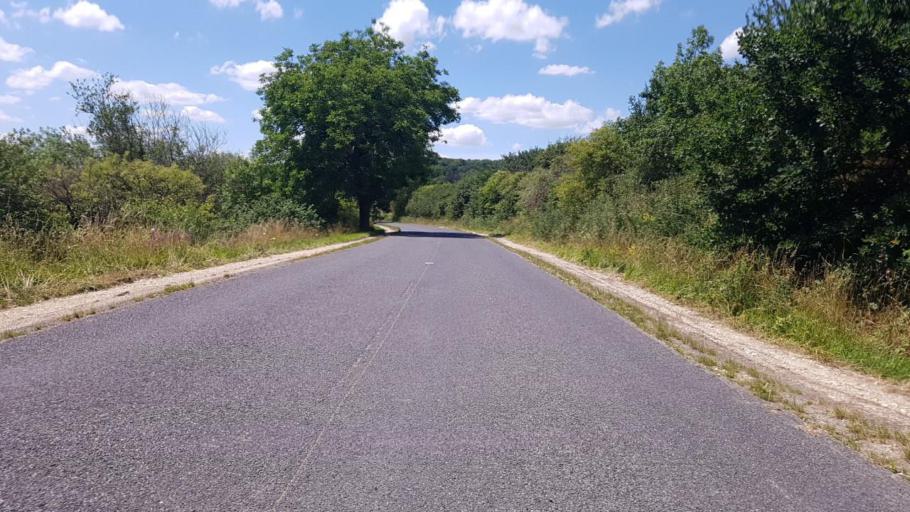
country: FR
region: Lorraine
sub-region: Departement de la Meuse
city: Ligny-en-Barrois
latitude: 48.6471
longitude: 5.4057
